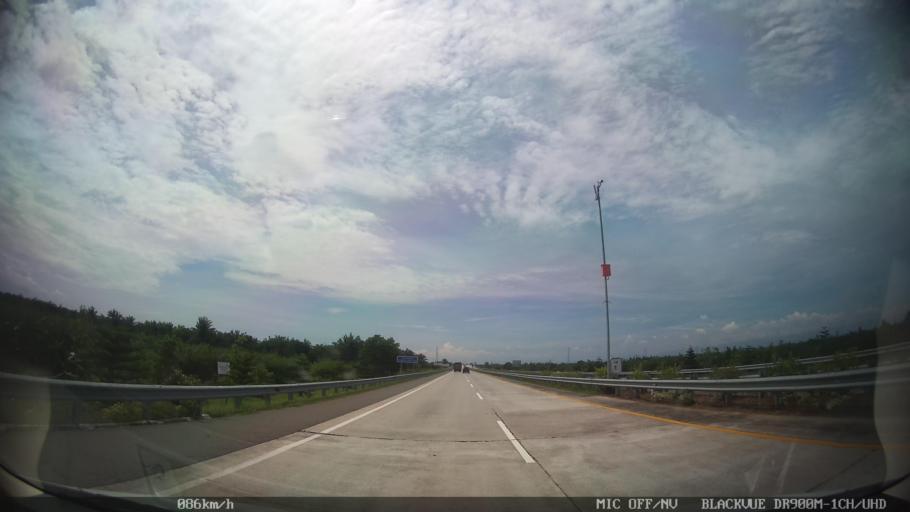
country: ID
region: North Sumatra
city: Percut
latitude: 3.5865
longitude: 98.8452
